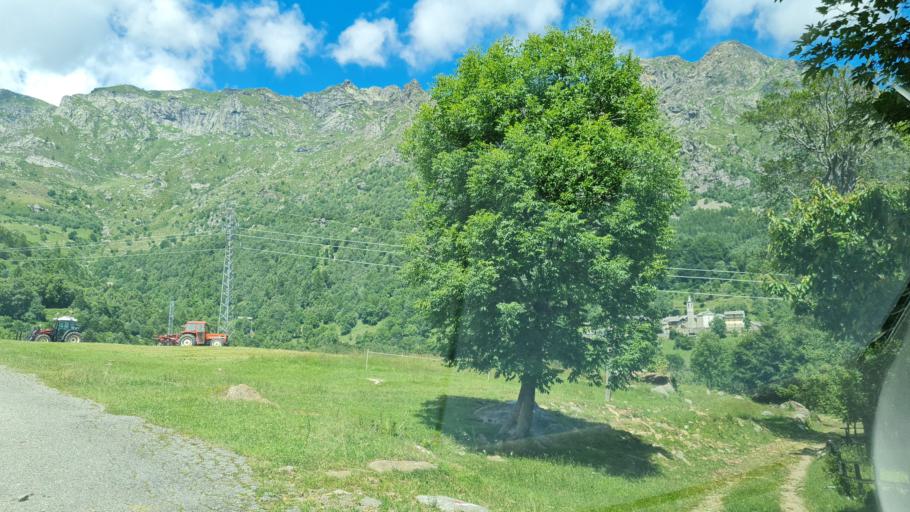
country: IT
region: Piedmont
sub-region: Provincia di Torino
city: Quincinetto
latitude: 45.5503
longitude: 7.7713
